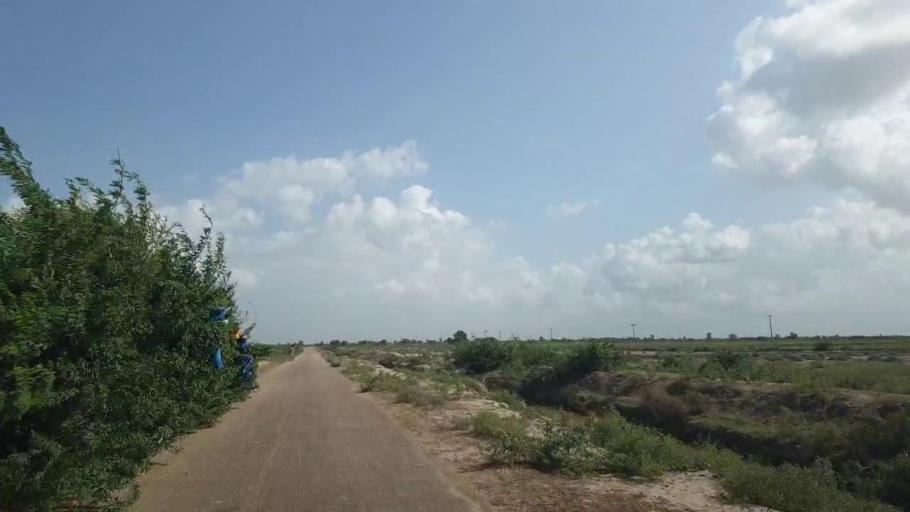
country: PK
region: Sindh
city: Kadhan
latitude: 24.5712
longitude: 69.0673
